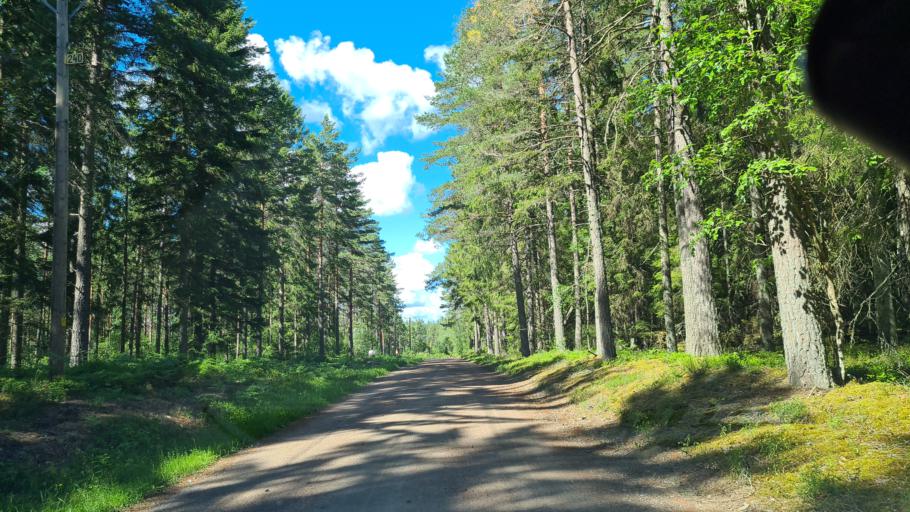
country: SE
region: OEstergoetland
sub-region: Norrkopings Kommun
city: Krokek
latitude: 58.6906
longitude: 16.4369
